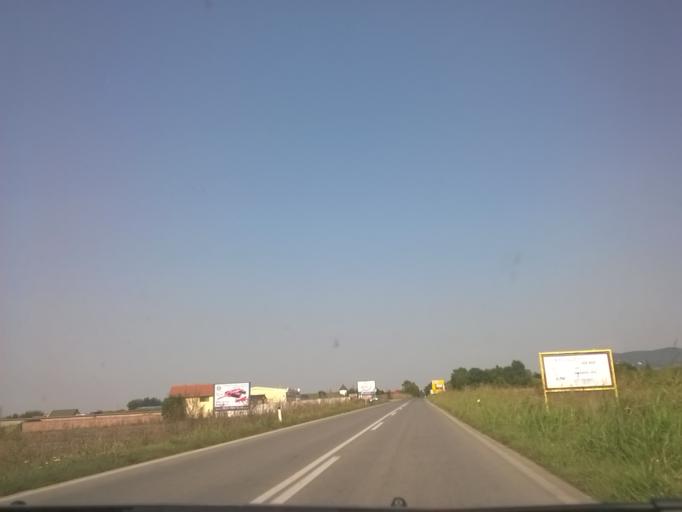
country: RS
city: Pavlis
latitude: 45.0991
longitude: 21.2706
